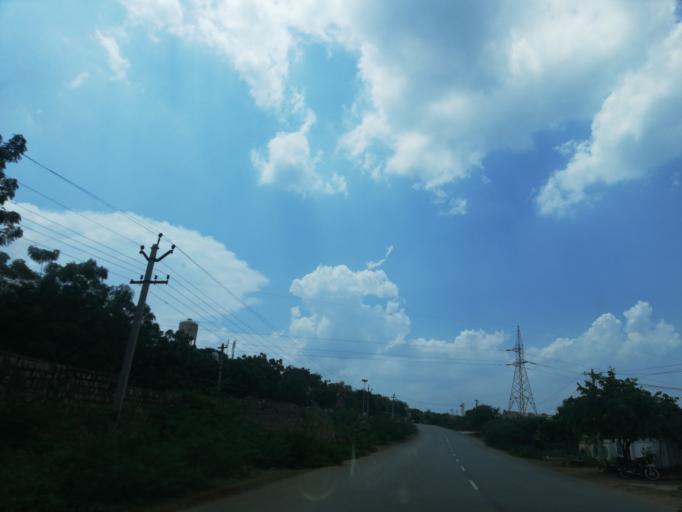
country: IN
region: Andhra Pradesh
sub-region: Guntur
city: Macherla
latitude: 16.5862
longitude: 79.3253
